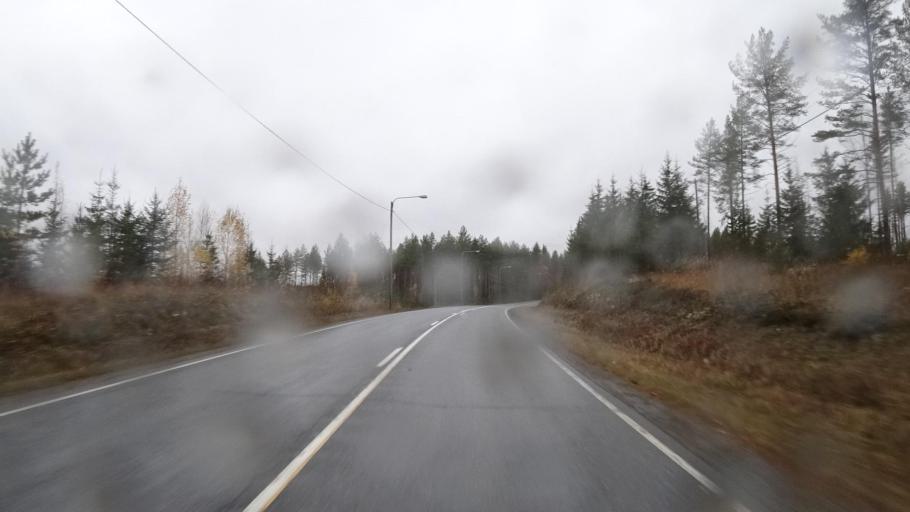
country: FI
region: Northern Savo
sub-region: Koillis-Savo
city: Tuusniemi
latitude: 62.8721
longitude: 28.3179
